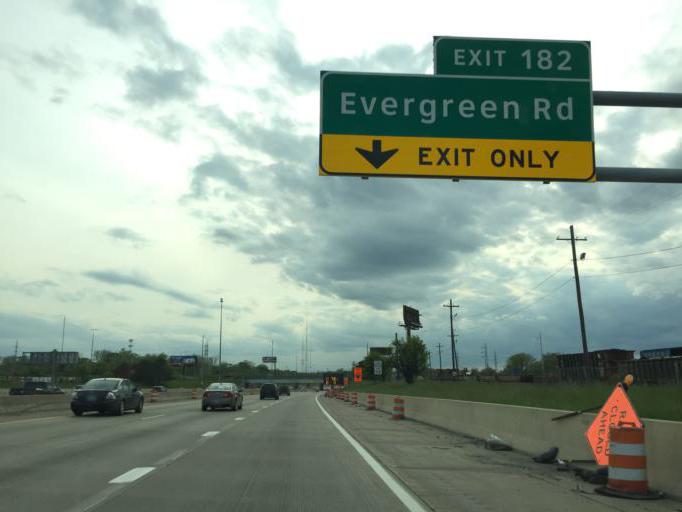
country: US
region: Michigan
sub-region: Wayne County
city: Dearborn Heights
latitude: 42.3783
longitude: -83.2258
